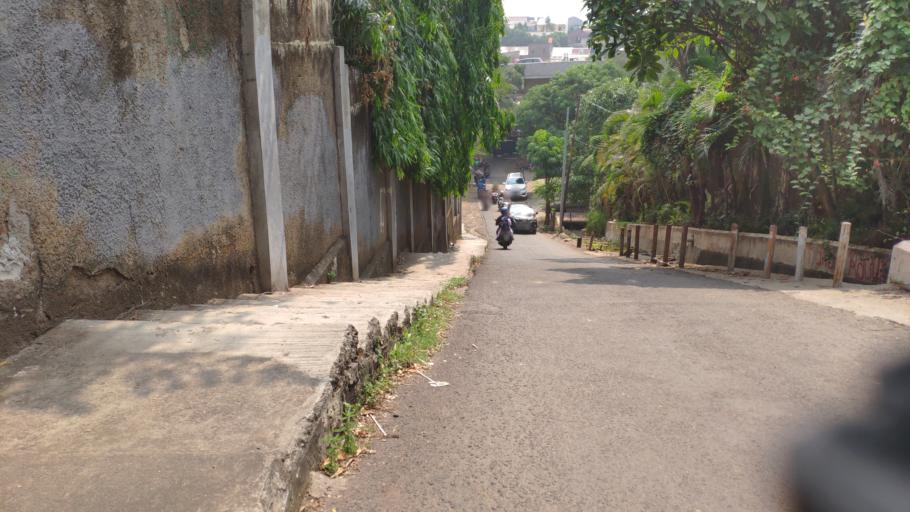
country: ID
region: West Java
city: Pamulang
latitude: -6.3024
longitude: 106.8027
